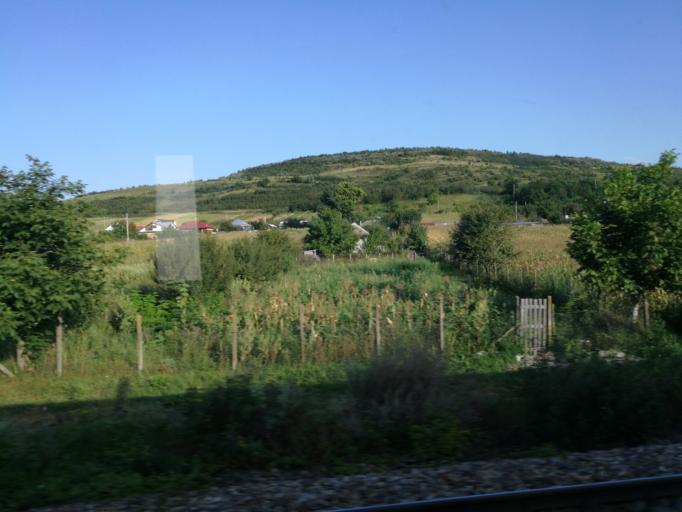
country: RO
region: Vaslui
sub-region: Comuna Banca
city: Banca
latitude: 46.3421
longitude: 27.7951
